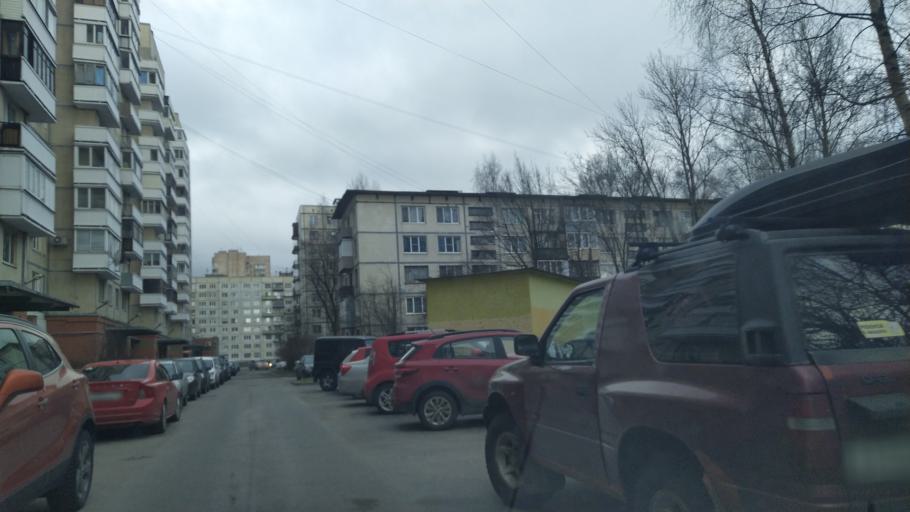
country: RU
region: St.-Petersburg
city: Grazhdanka
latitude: 60.0398
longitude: 30.3955
